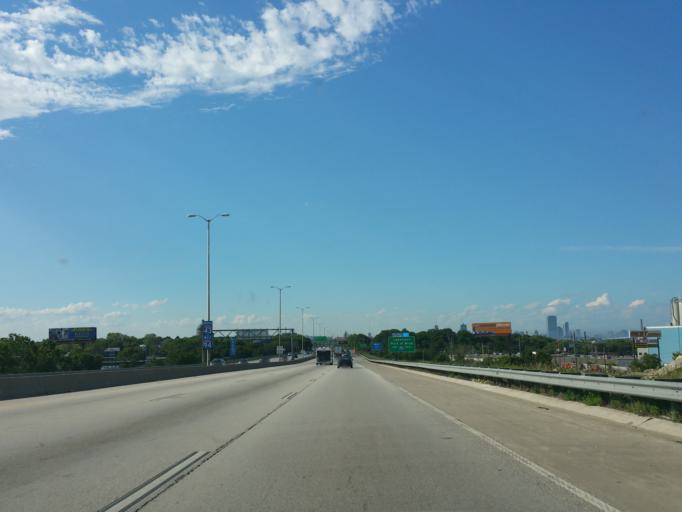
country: US
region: Wisconsin
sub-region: Milwaukee County
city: Saint Francis
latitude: 42.9898
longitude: -87.9139
